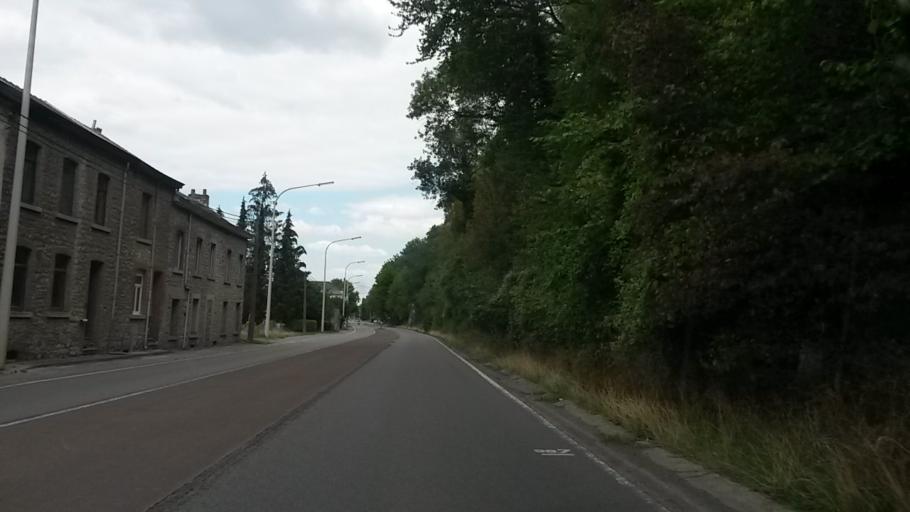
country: BE
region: Wallonia
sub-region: Province de Liege
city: Wanze
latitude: 50.5179
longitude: 5.1925
